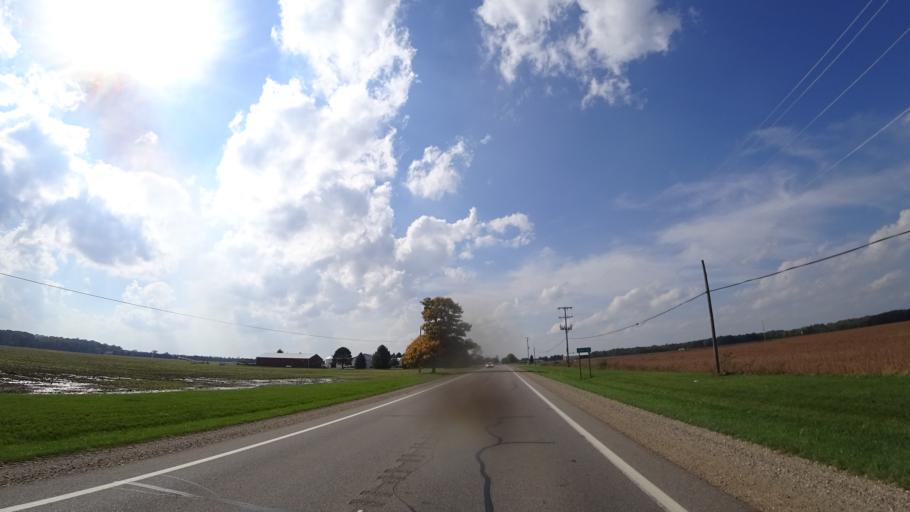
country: US
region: Michigan
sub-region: Saint Joseph County
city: Centreville
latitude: 42.0063
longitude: -85.4811
